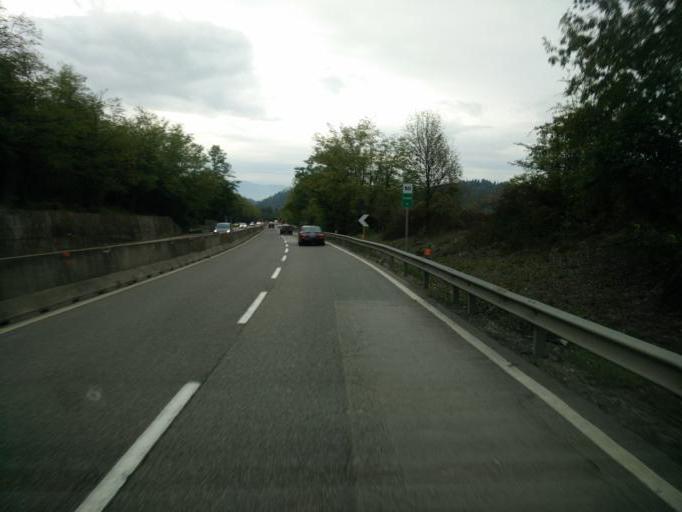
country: IT
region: Tuscany
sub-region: Province of Florence
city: San Casciano in Val di Pesa
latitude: 43.6663
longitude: 11.2093
